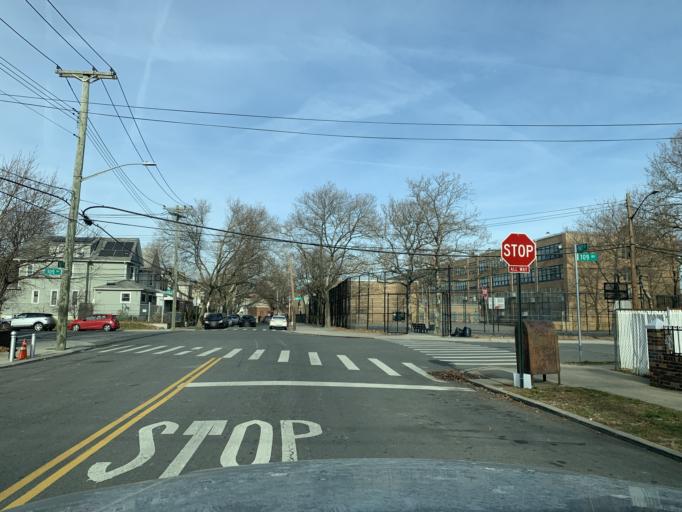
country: US
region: New York
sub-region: Queens County
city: Jamaica
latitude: 40.6958
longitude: -73.7864
